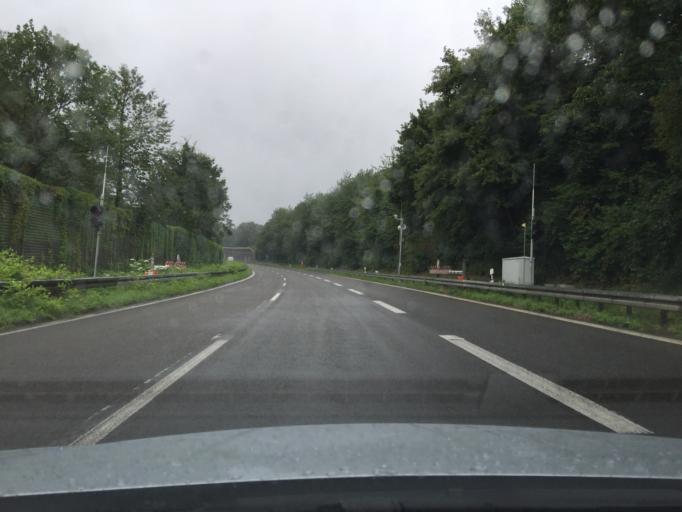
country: DE
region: North Rhine-Westphalia
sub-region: Regierungsbezirk Dusseldorf
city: Velbert
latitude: 51.3477
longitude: 7.0264
